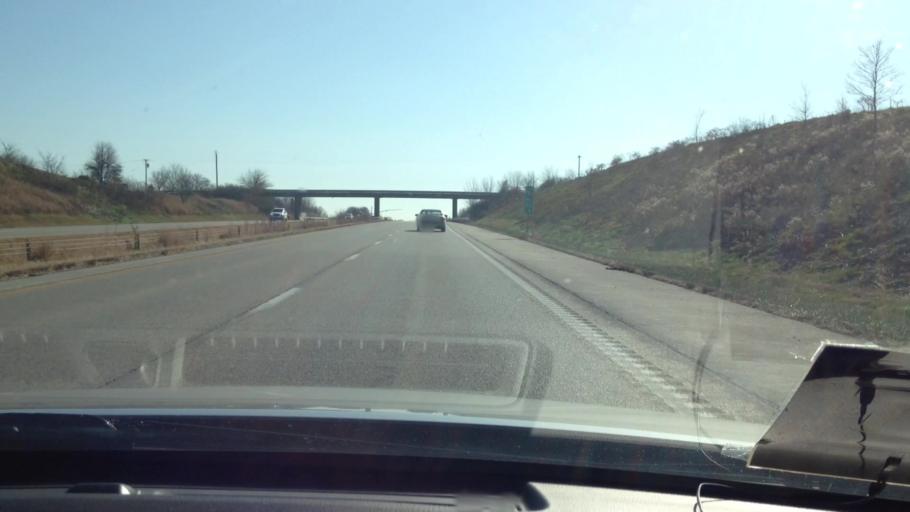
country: US
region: Missouri
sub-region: Platte County
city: Platte City
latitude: 39.4208
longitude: -94.7899
